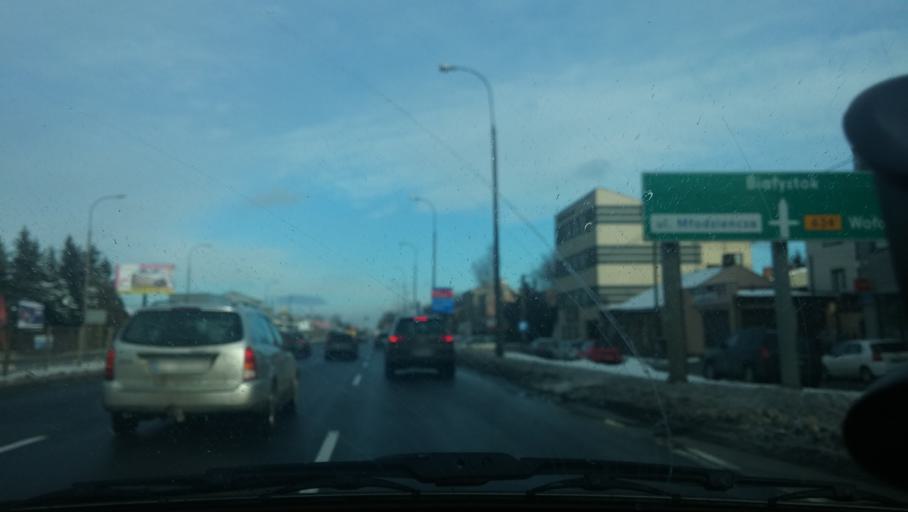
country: PL
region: Masovian Voivodeship
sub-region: Warszawa
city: Targowek
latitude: 52.2846
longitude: 21.0735
